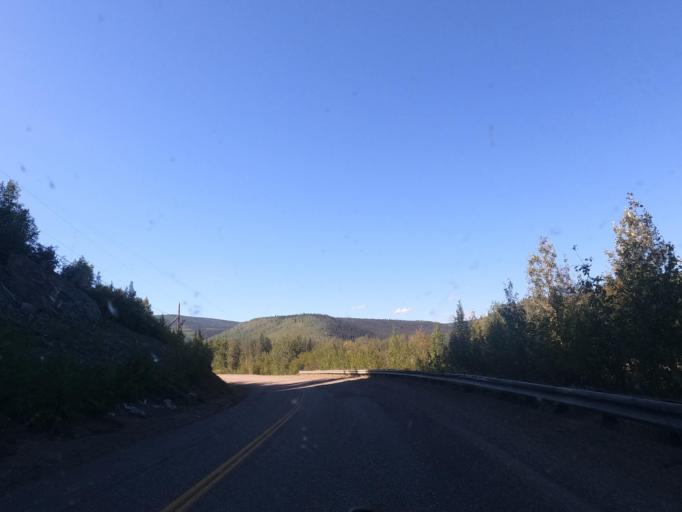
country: CA
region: Yukon
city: Dawson City
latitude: 64.0610
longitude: -139.0711
